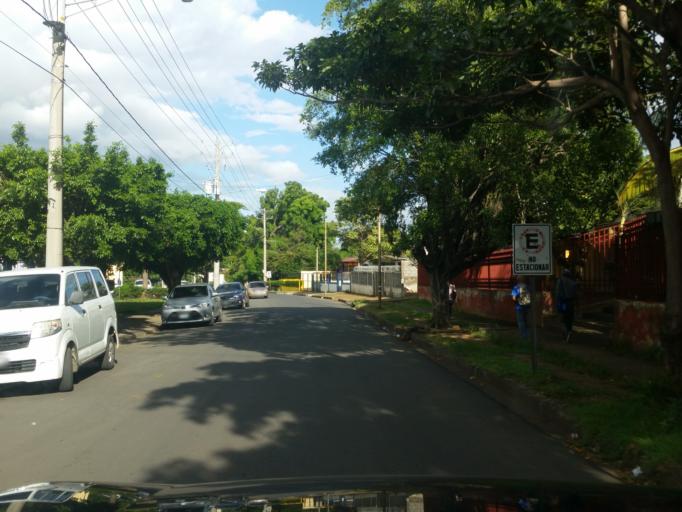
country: NI
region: Managua
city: Ciudad Sandino
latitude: 12.1259
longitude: -86.3076
